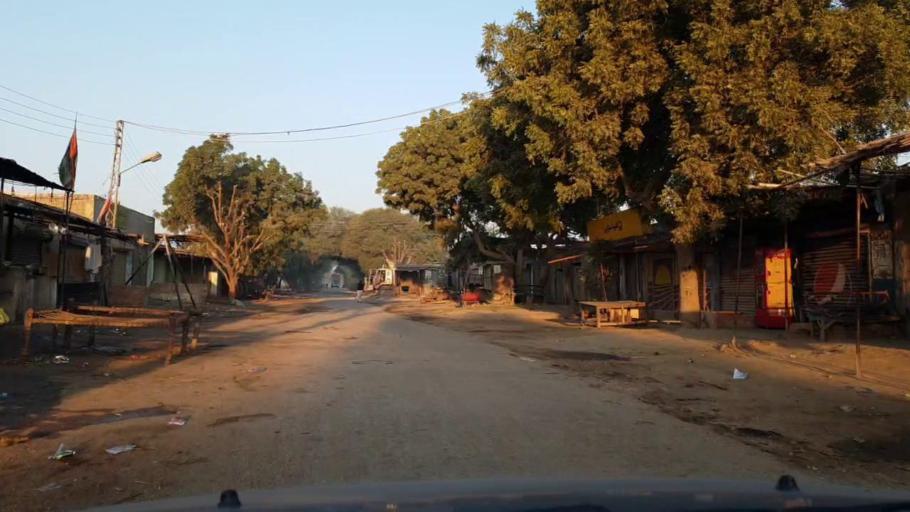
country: PK
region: Sindh
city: Chambar
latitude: 25.2614
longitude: 68.6578
